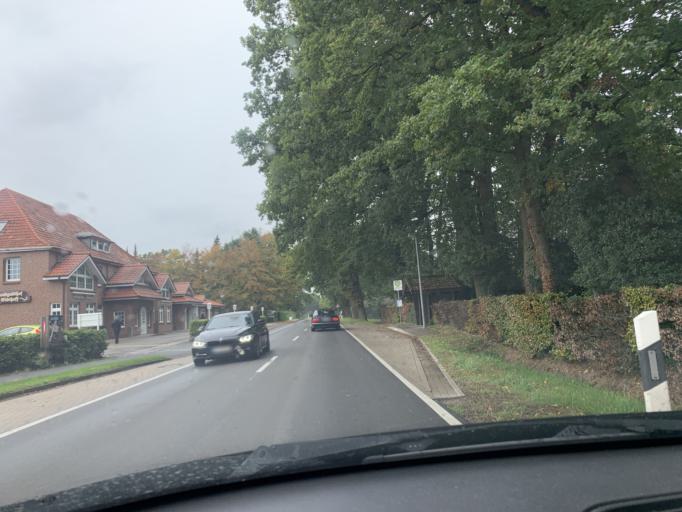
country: DE
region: Lower Saxony
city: Bad Zwischenahn
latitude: 53.1621
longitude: 8.0771
